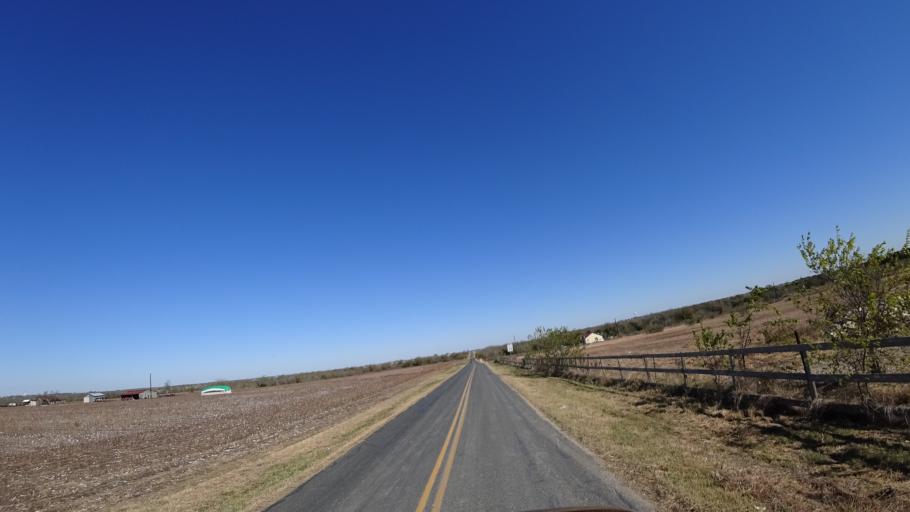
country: US
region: Texas
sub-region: Travis County
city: Garfield
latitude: 30.0911
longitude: -97.6246
